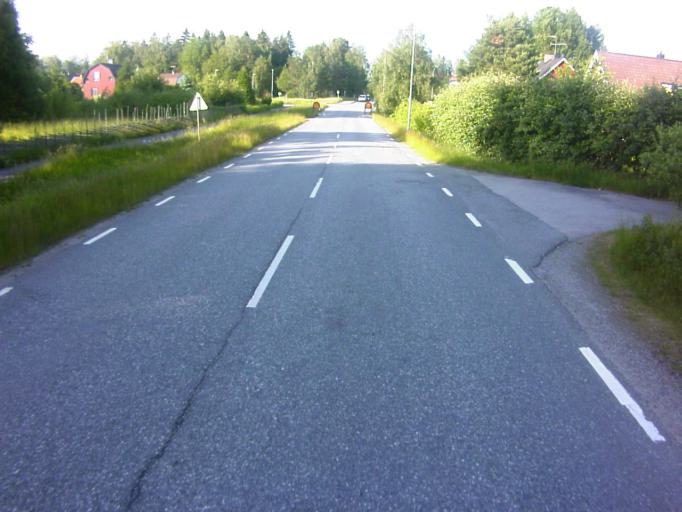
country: SE
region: Soedermanland
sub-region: Eskilstuna Kommun
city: Skogstorp
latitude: 59.3185
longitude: 16.4732
